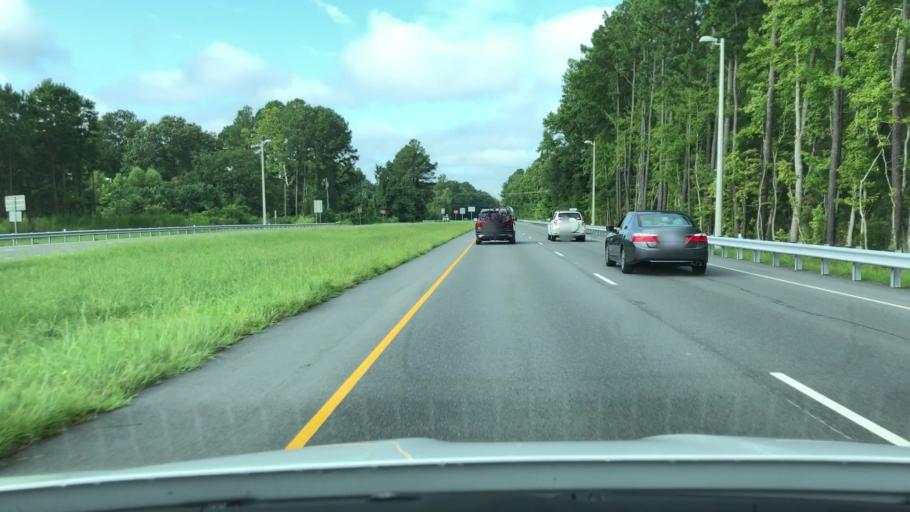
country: US
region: Virginia
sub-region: City of Chesapeake
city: Chesapeake
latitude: 36.7166
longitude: -76.3198
